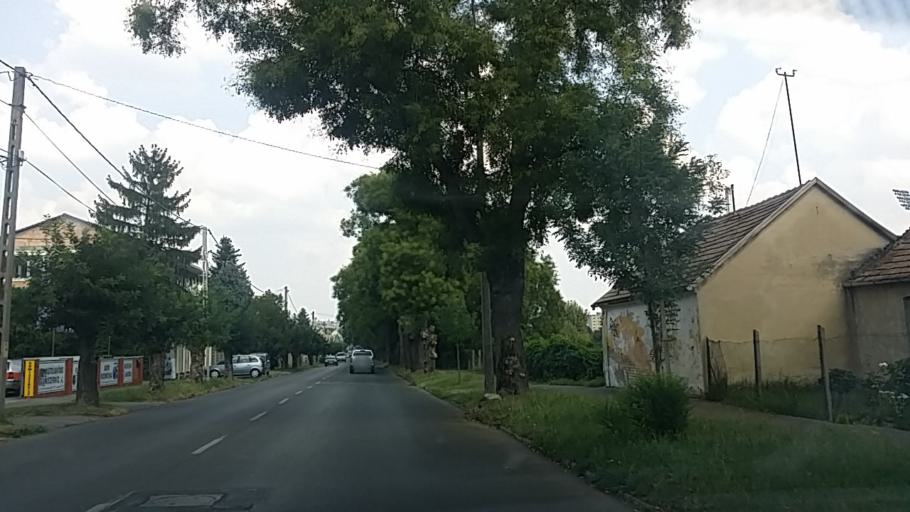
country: HU
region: Baranya
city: Pecs
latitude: 46.0685
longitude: 18.1929
